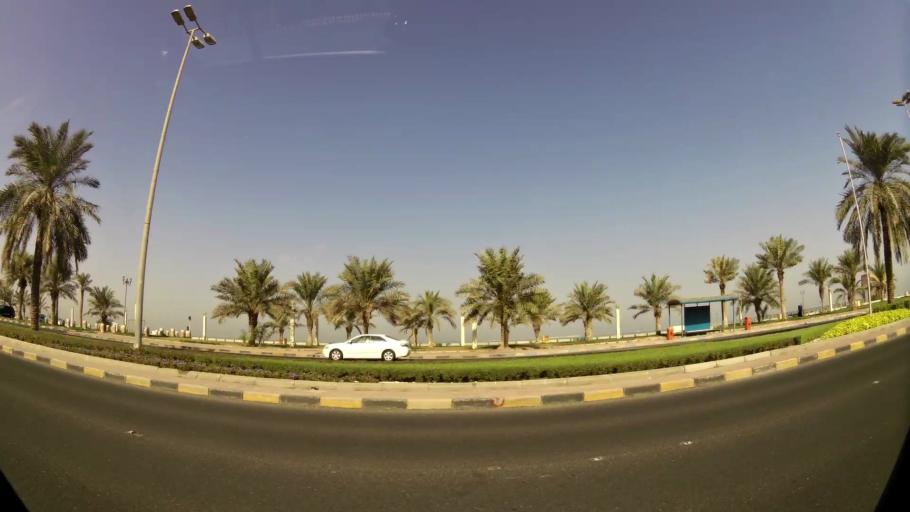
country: KW
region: Al Asimah
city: Kuwait City
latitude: 29.3715
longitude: 47.9636
